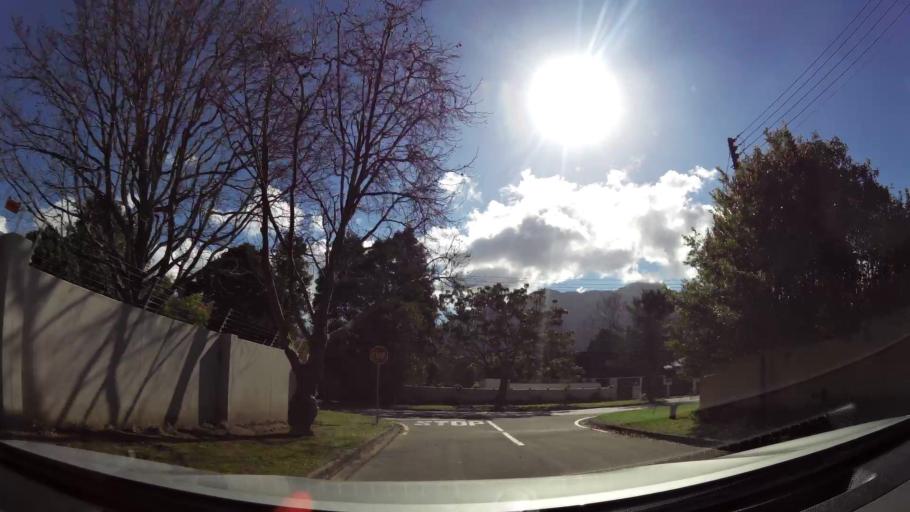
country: ZA
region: Western Cape
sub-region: Eden District Municipality
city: George
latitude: -33.9495
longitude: 22.4408
